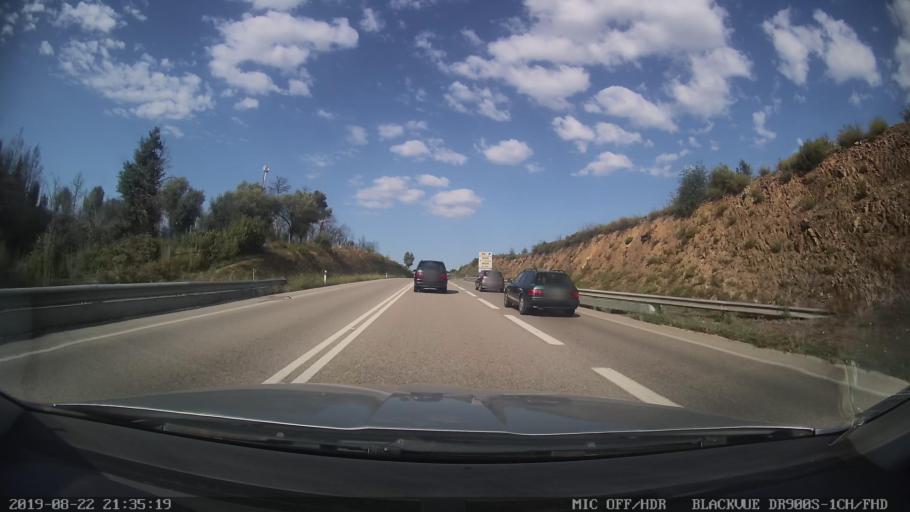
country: PT
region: Leiria
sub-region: Pedrogao Grande
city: Pedrogao Grande
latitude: 39.9250
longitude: -8.2041
